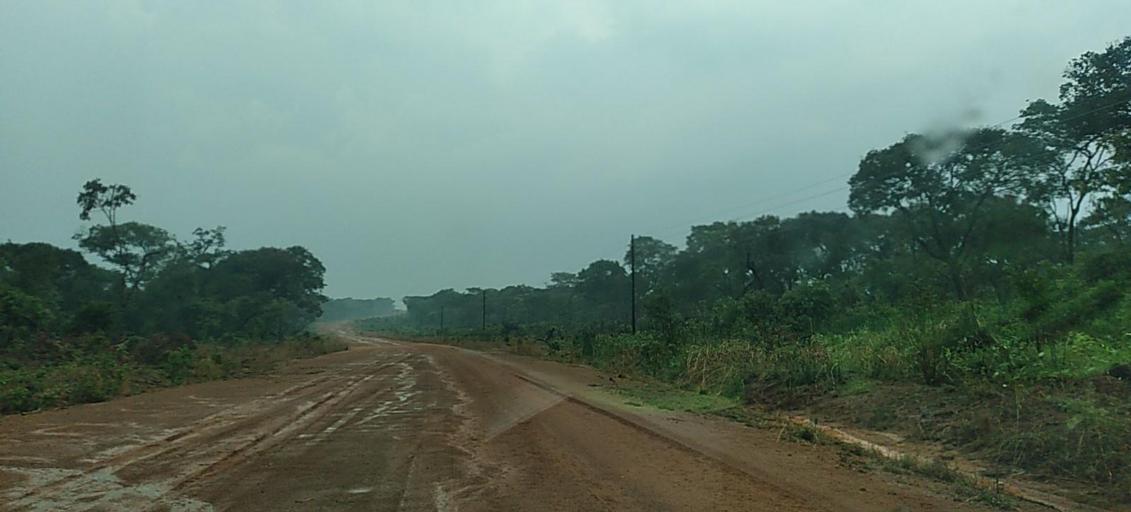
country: ZM
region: North-Western
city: Mwinilunga
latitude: -11.5937
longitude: 24.3895
